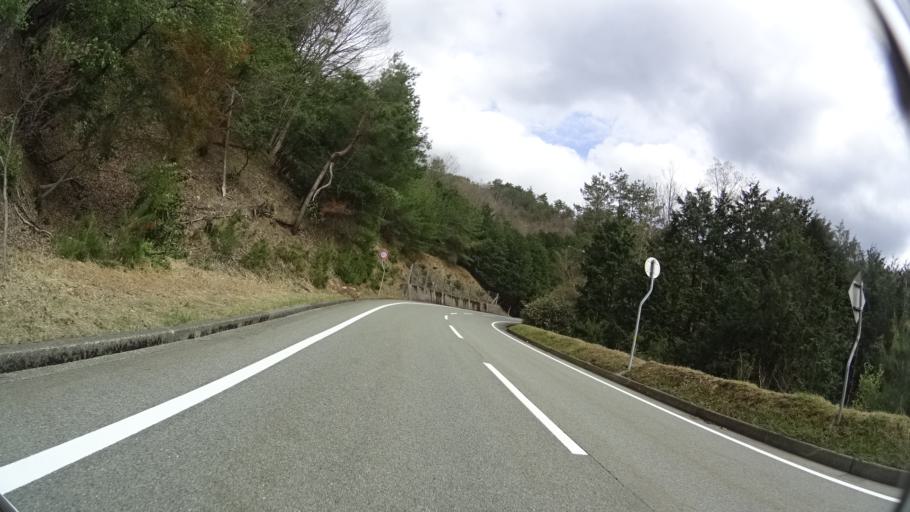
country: JP
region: Hyogo
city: Toyooka
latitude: 35.5052
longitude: 134.9011
